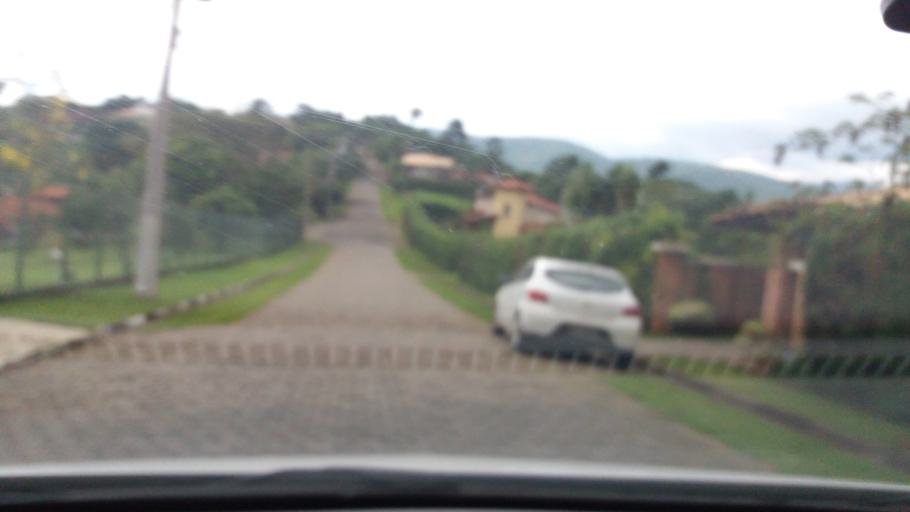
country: BR
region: Sao Paulo
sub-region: Bom Jesus Dos Perdoes
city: Bom Jesus dos Perdoes
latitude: -23.1670
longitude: -46.4636
